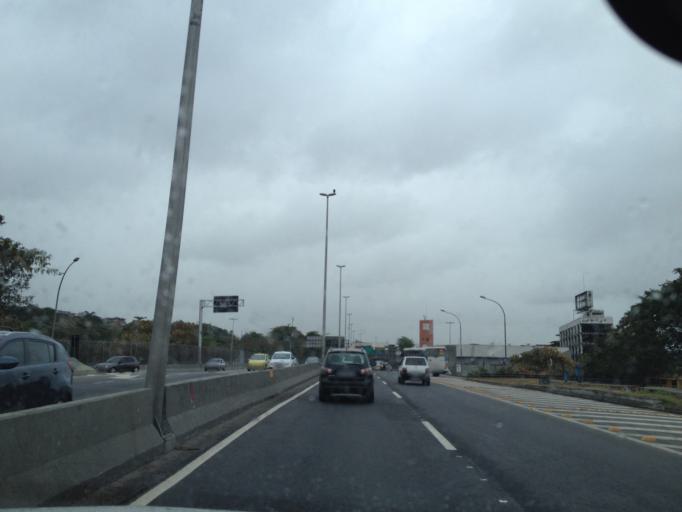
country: BR
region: Rio de Janeiro
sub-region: Rio De Janeiro
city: Rio de Janeiro
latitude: -22.8703
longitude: -43.2447
